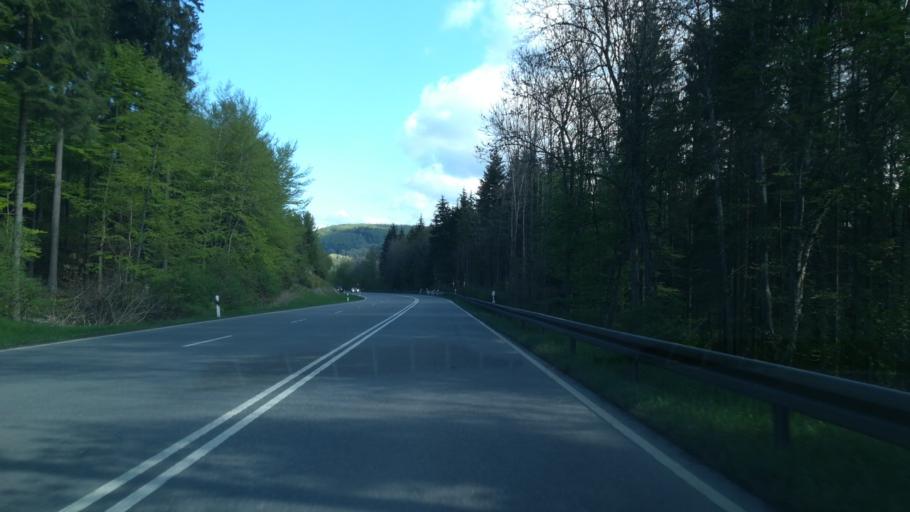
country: DE
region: Baden-Wuerttemberg
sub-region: Freiburg Region
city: Blumberg
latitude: 47.8313
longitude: 8.5642
